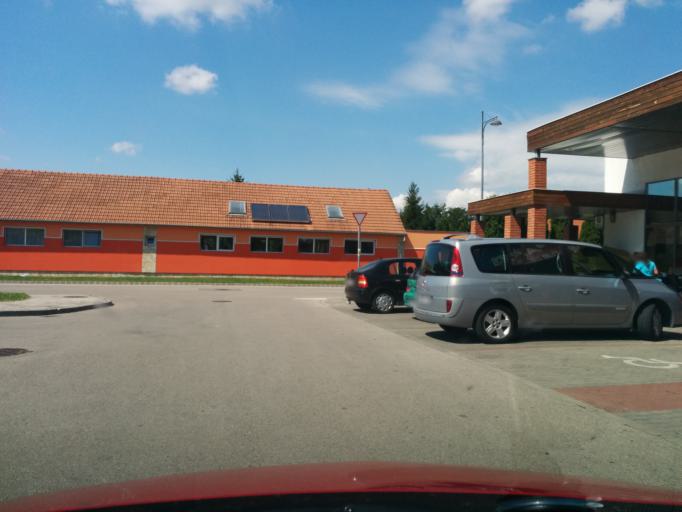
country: HU
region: Komarom-Esztergom
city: Komarom
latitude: 47.7468
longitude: 18.1100
